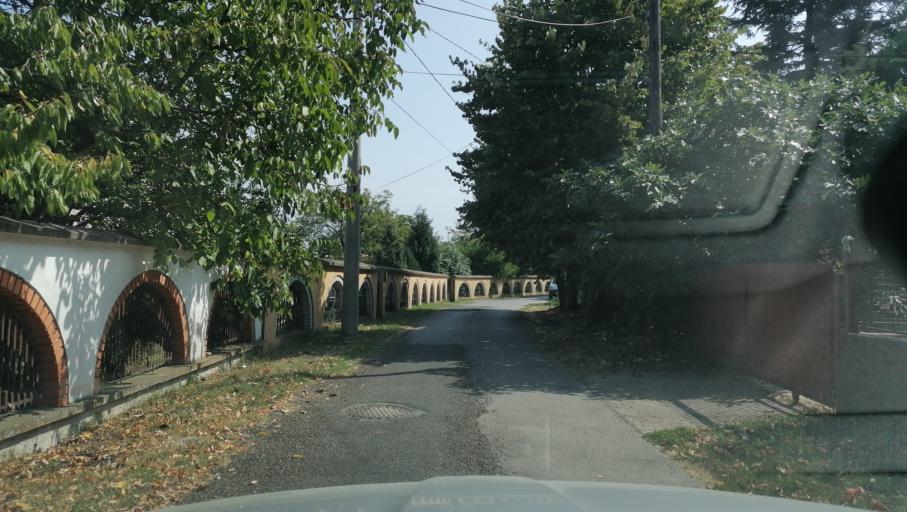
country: RS
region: Central Serbia
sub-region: Belgrade
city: Zvezdara
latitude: 44.7007
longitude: 20.5525
